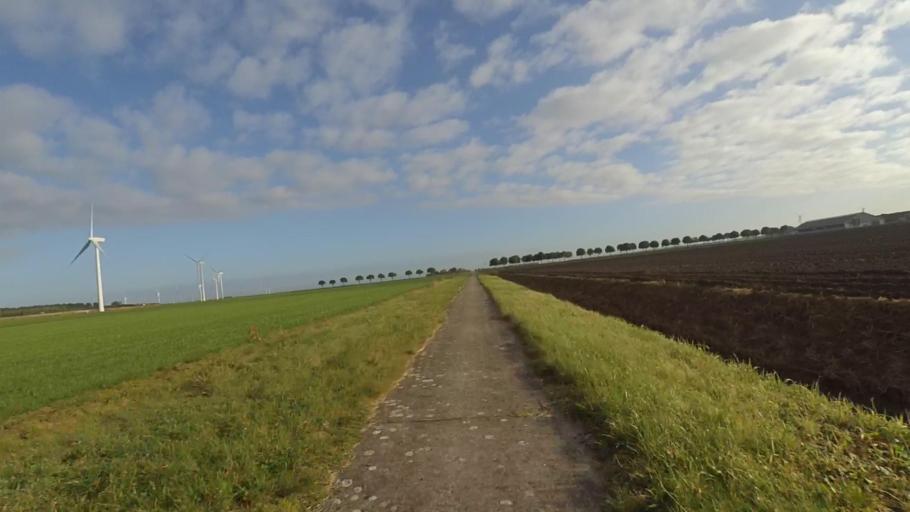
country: NL
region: Utrecht
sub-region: Gemeente Bunschoten
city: Spakenburg
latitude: 52.3154
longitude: 5.3405
